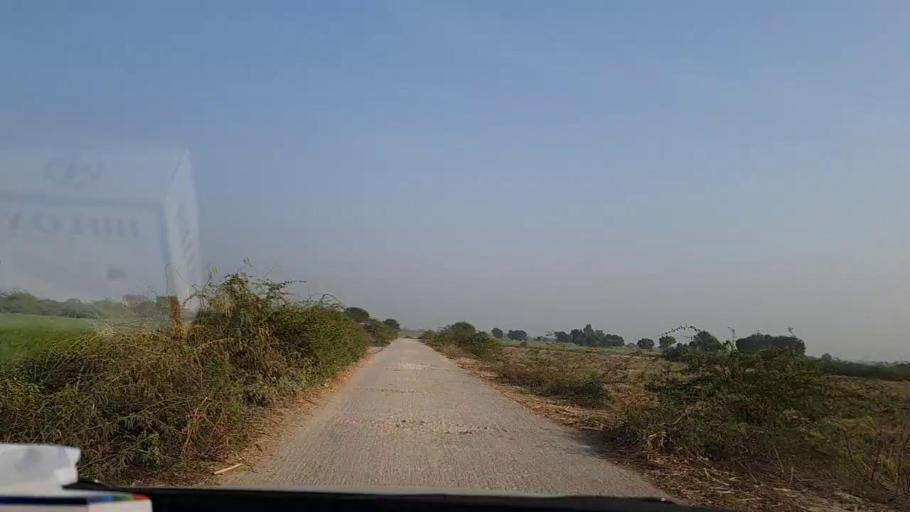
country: PK
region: Sindh
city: Tando Ghulam Ali
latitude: 25.2138
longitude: 68.8854
